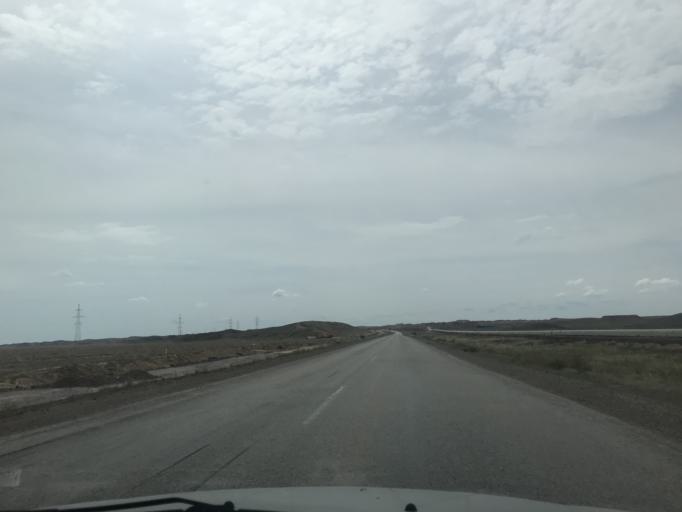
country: KZ
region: Zhambyl
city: Mynaral
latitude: 45.3790
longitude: 73.6535
